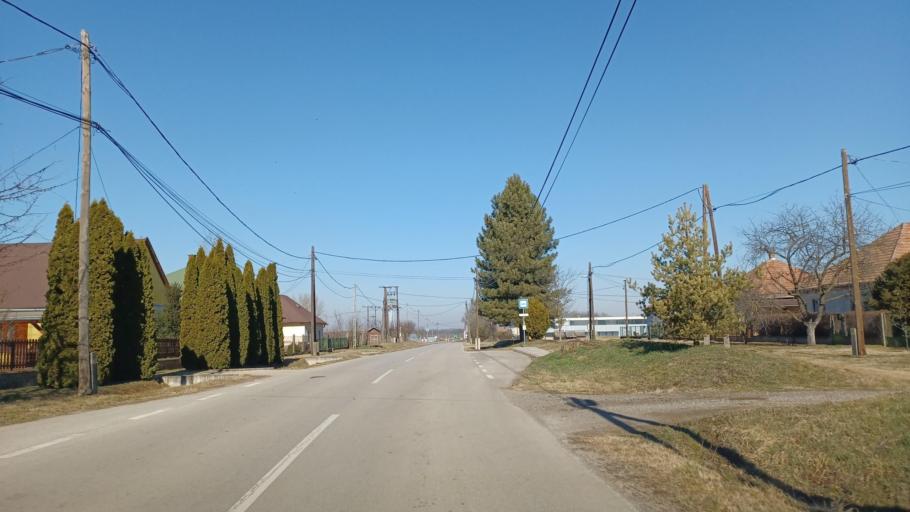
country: HU
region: Tolna
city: Tengelic
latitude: 46.5444
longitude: 18.7006
